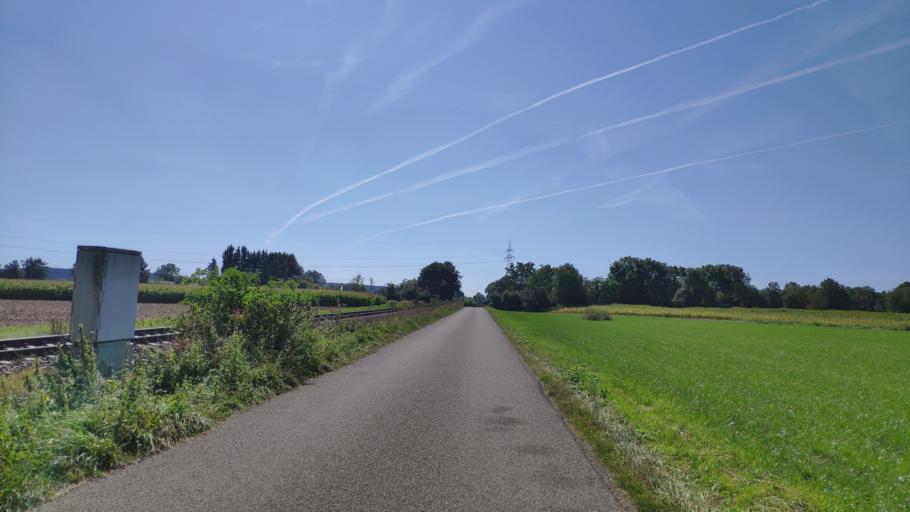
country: DE
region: Bavaria
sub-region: Swabia
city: Neu-Ulm
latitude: 48.3697
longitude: 10.0319
